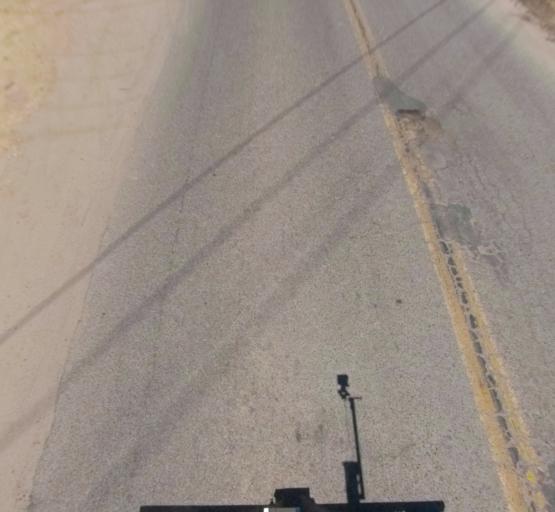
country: US
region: California
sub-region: Madera County
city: Madera
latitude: 36.9867
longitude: -120.0382
